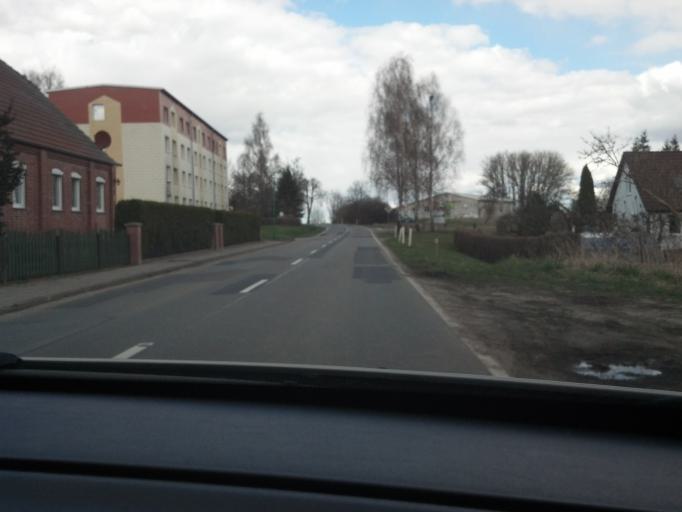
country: DE
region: Mecklenburg-Vorpommern
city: Loitz
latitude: 53.4222
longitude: 13.3528
